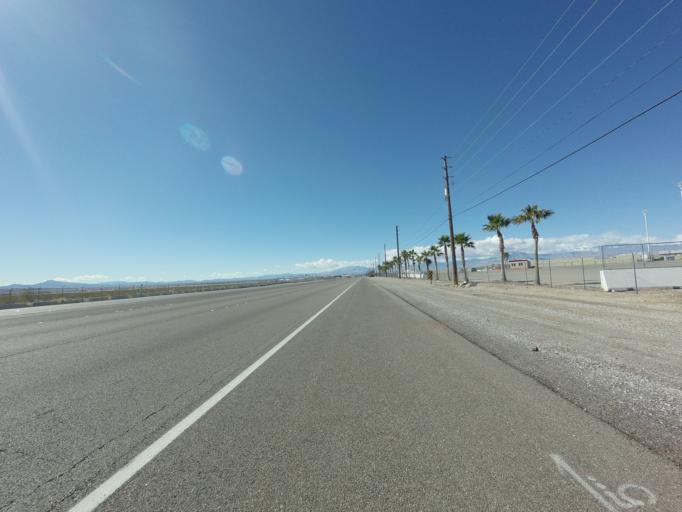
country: US
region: Nevada
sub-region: Clark County
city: Nellis Air Force Base
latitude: 36.2617
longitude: -115.0183
